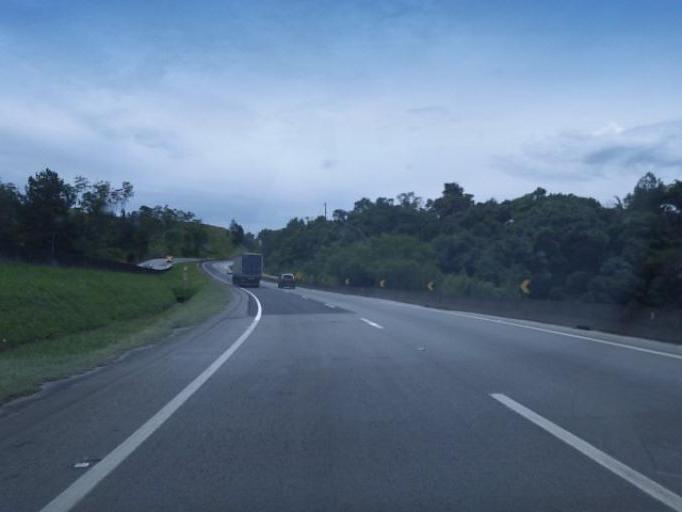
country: BR
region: Sao Paulo
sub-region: Juquitiba
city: Juquitiba
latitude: -23.9353
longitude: -47.0755
